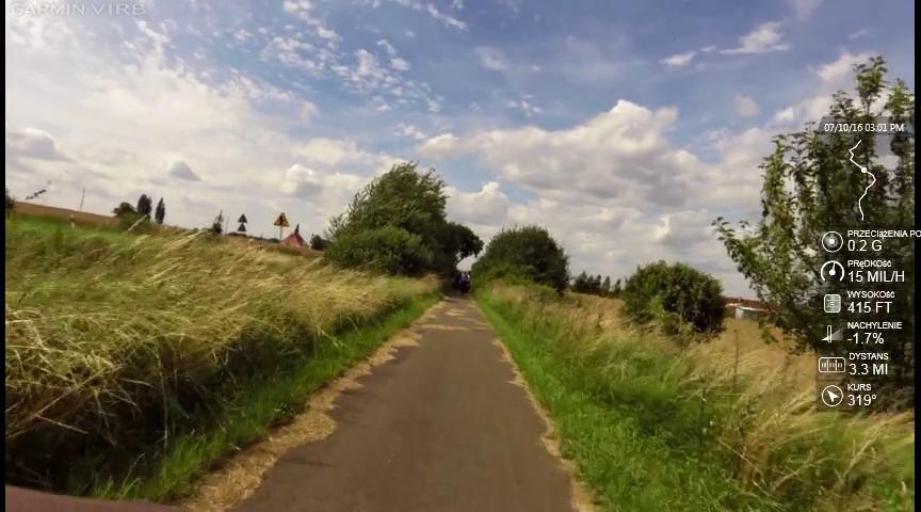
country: PL
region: West Pomeranian Voivodeship
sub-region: Powiat gryfinski
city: Banie
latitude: 53.1111
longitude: 14.6337
